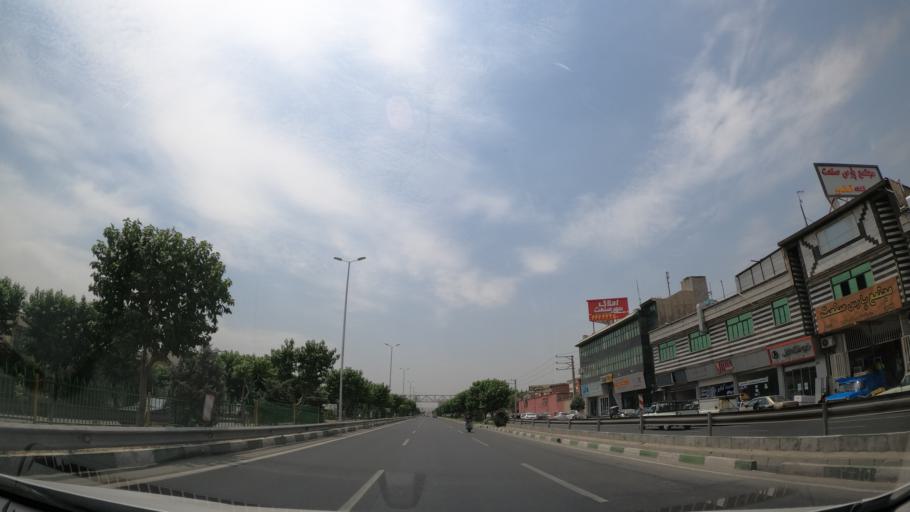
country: IR
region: Tehran
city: Tehran
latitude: 35.6752
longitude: 51.3185
